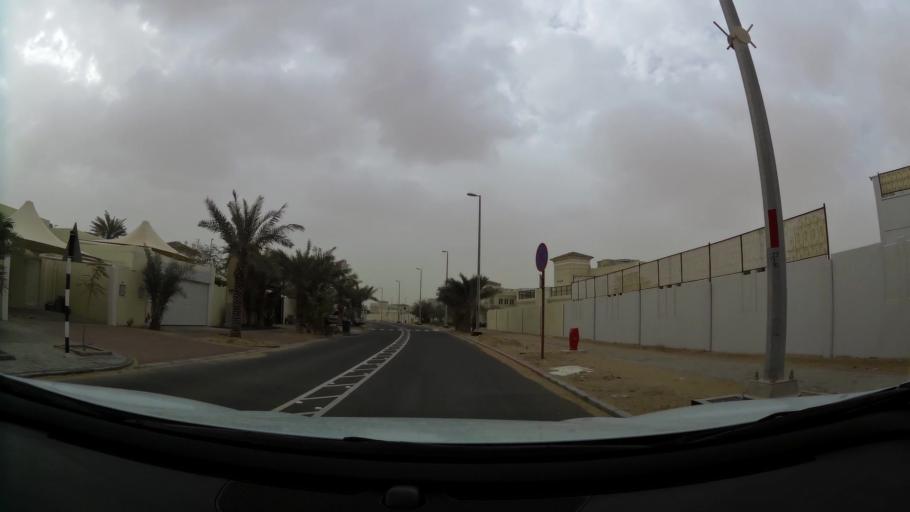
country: AE
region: Abu Dhabi
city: Abu Dhabi
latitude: 24.4414
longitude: 54.7125
